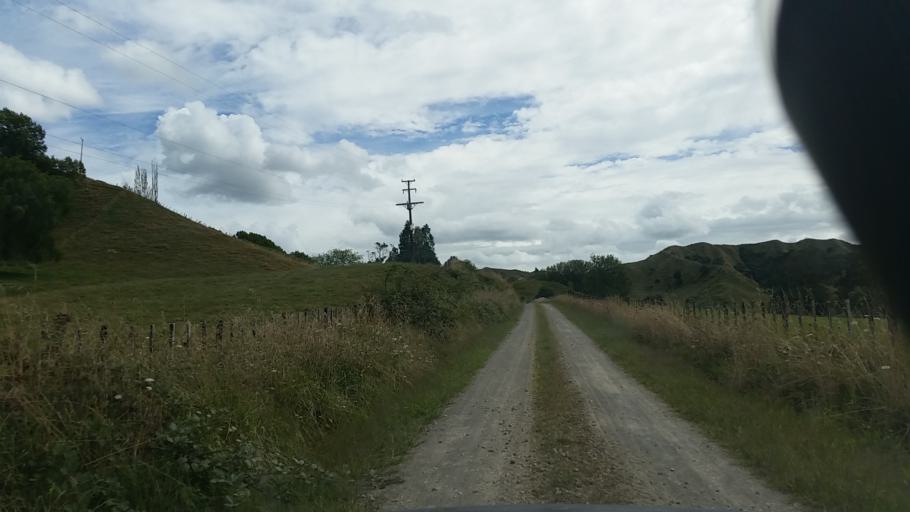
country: NZ
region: Taranaki
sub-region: South Taranaki District
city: Eltham
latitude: -39.2572
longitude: 174.5649
